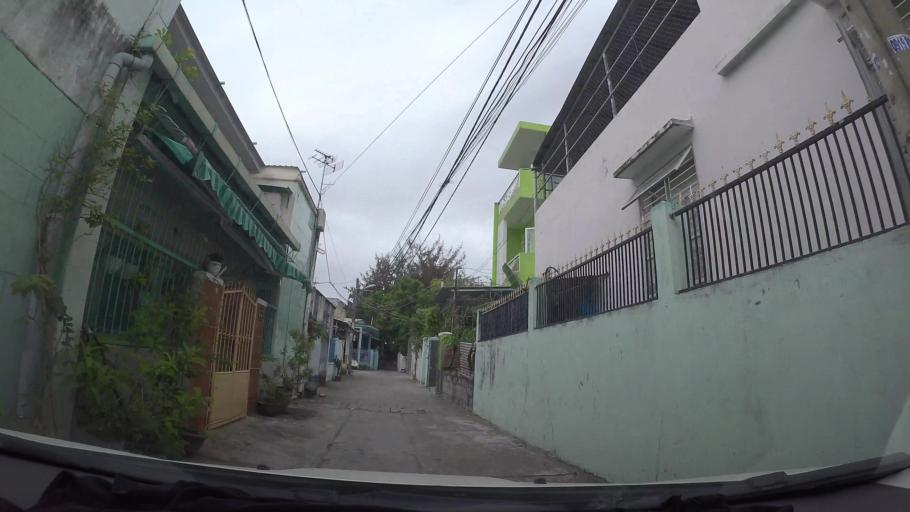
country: VN
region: Da Nang
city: Lien Chieu
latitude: 16.1217
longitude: 108.1161
